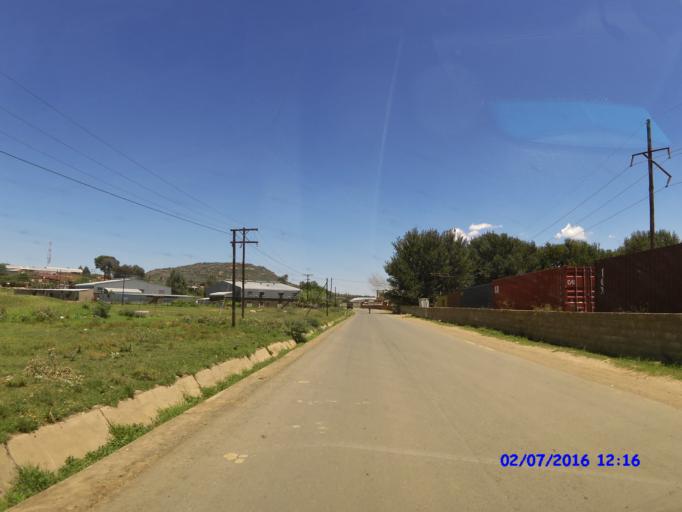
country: LS
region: Maseru
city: Maseru
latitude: -29.2968
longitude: 27.4634
